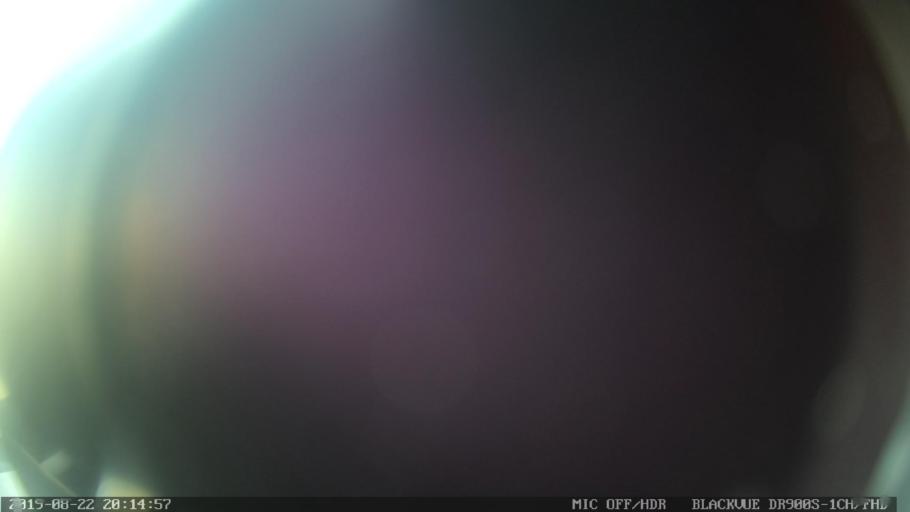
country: PT
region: Guarda
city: Alcains
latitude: 39.9214
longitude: -7.4349
